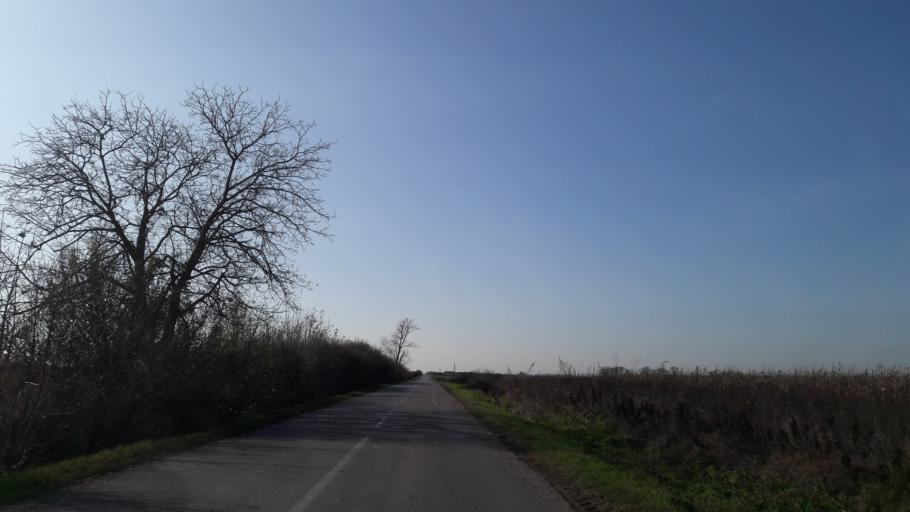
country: HR
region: Osjecko-Baranjska
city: Tenja
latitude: 45.4912
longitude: 18.7338
